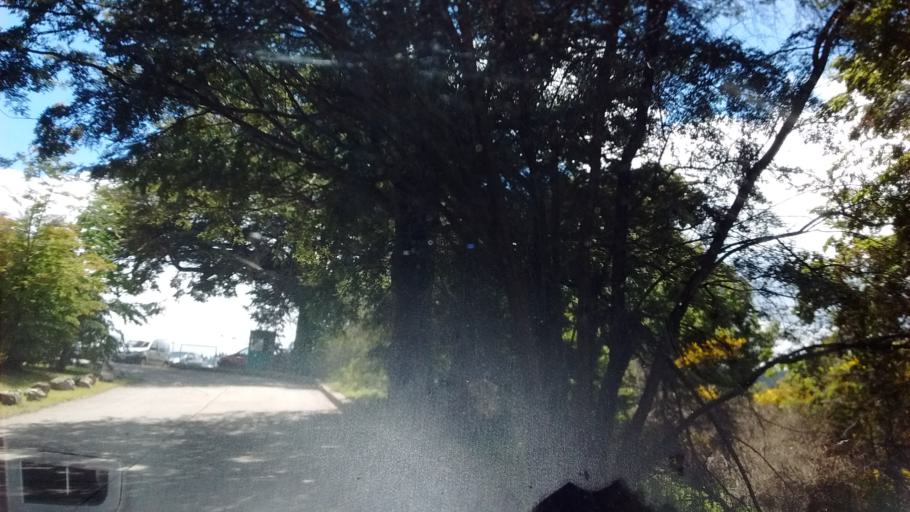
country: AR
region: Rio Negro
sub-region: Departamento de Bariloche
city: San Carlos de Bariloche
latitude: -41.0591
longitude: -71.5305
